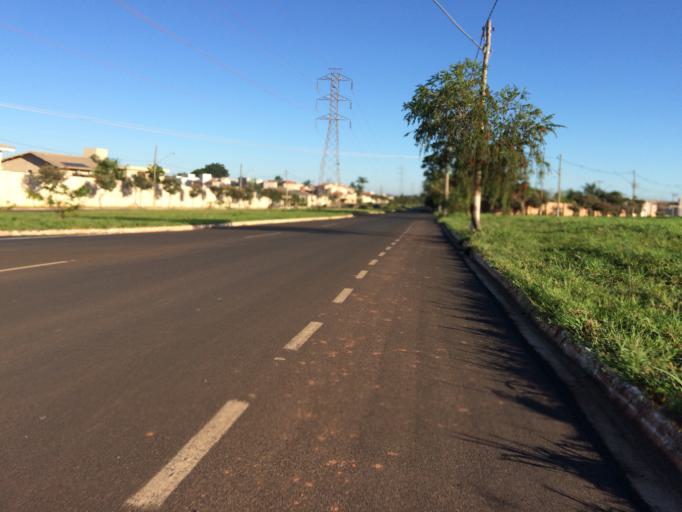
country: BR
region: Sao Paulo
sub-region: Matao
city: Matao
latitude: -21.6234
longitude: -48.3602
